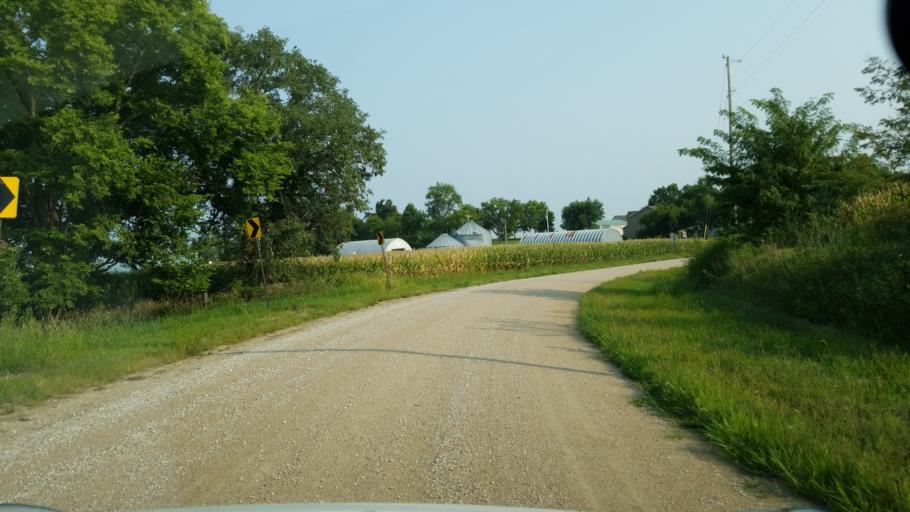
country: US
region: Nebraska
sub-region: Sarpy County
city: Offutt Air Force Base
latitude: 41.0762
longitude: -95.9331
